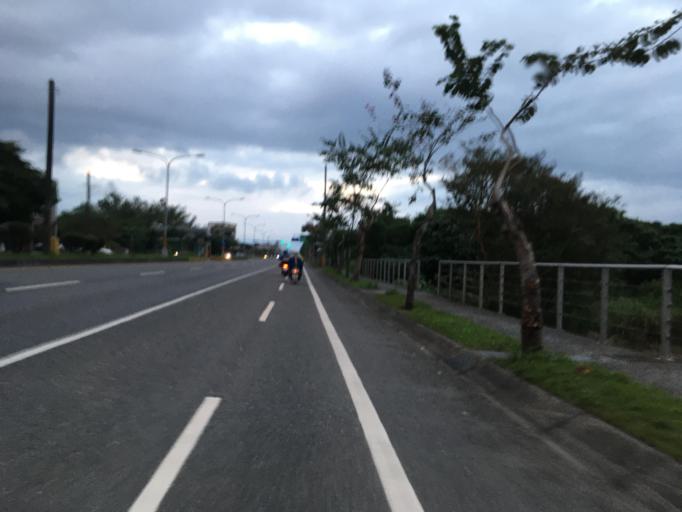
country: TW
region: Taiwan
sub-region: Yilan
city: Yilan
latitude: 24.6178
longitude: 121.8456
